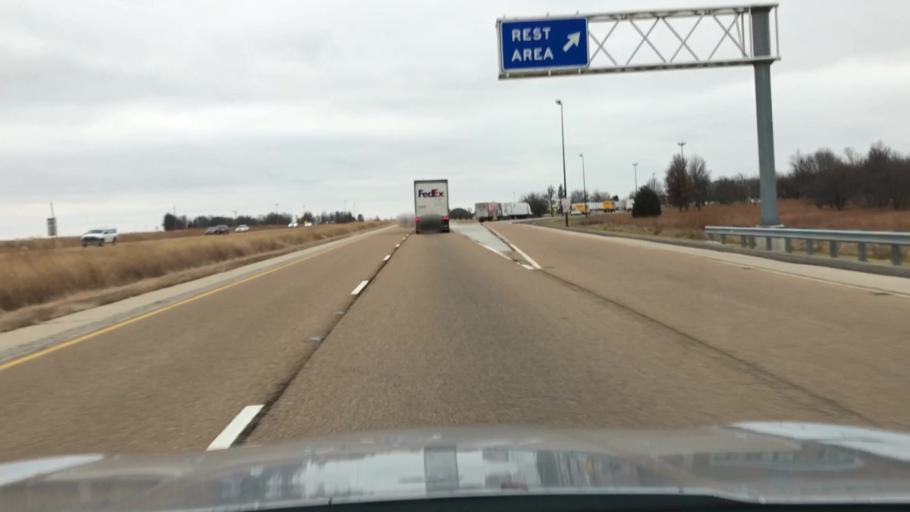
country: US
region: Illinois
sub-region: Montgomery County
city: Raymond
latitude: 39.3555
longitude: -89.6430
